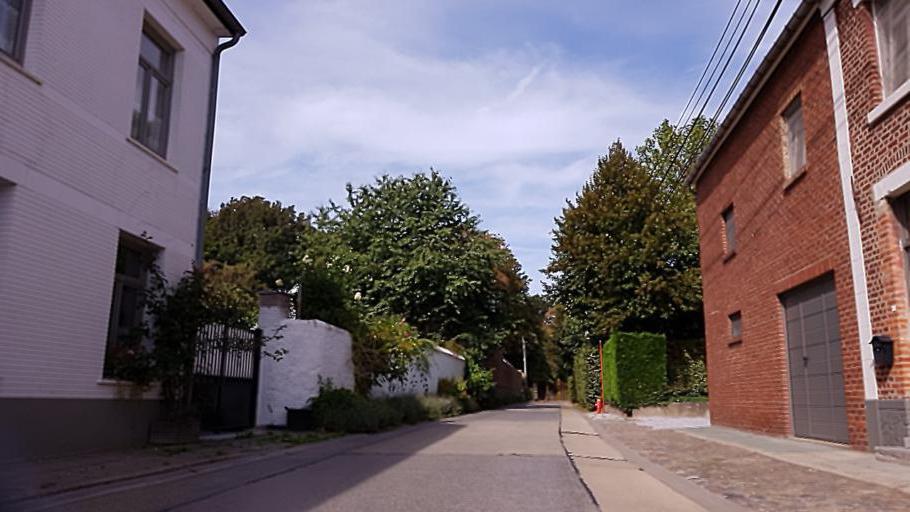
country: BE
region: Wallonia
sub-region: Province du Brabant Wallon
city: Grez-Doiceau
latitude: 50.7603
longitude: 4.6959
